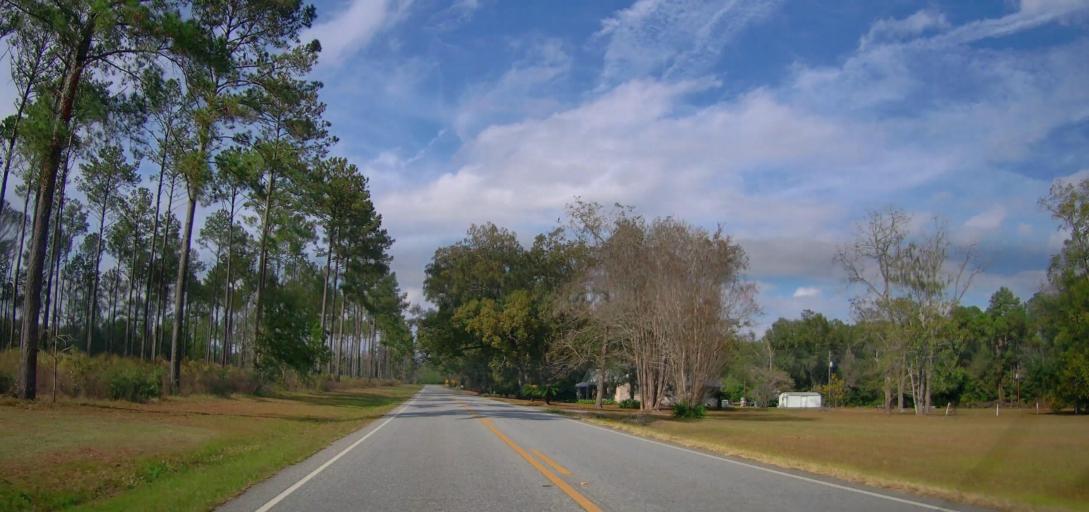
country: US
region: Georgia
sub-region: Thomas County
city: Thomasville
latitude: 30.9460
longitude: -84.0320
